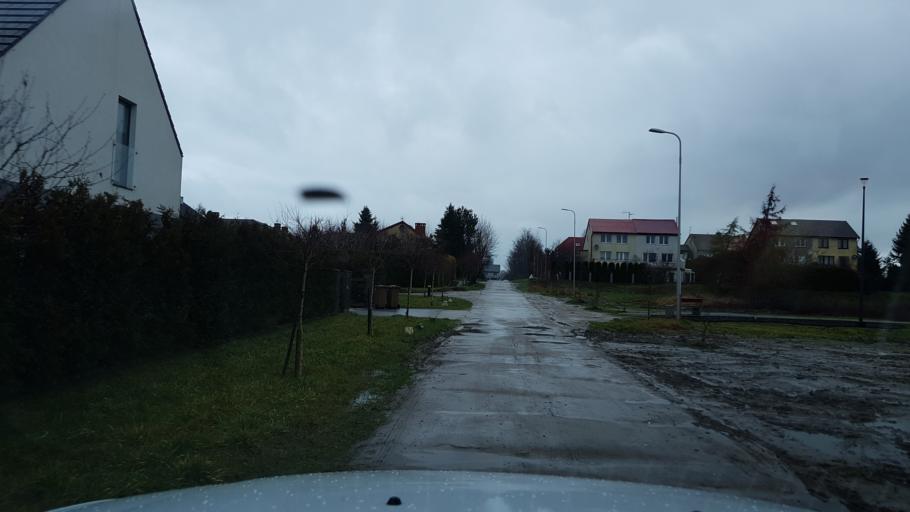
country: PL
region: West Pomeranian Voivodeship
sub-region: Powiat slawienski
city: Darlowo
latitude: 54.4258
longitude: 16.4249
